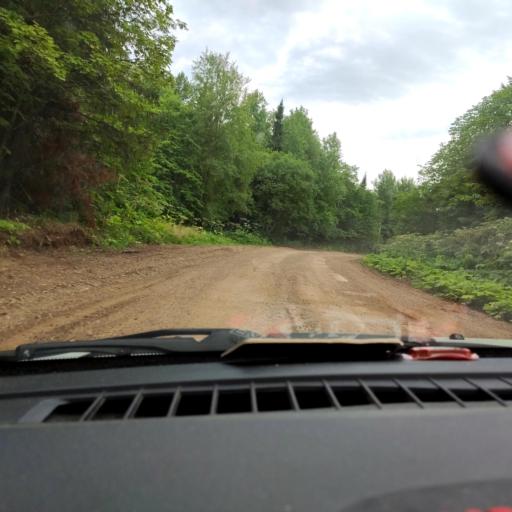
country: RU
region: Perm
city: Kultayevo
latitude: 57.8116
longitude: 56.0041
